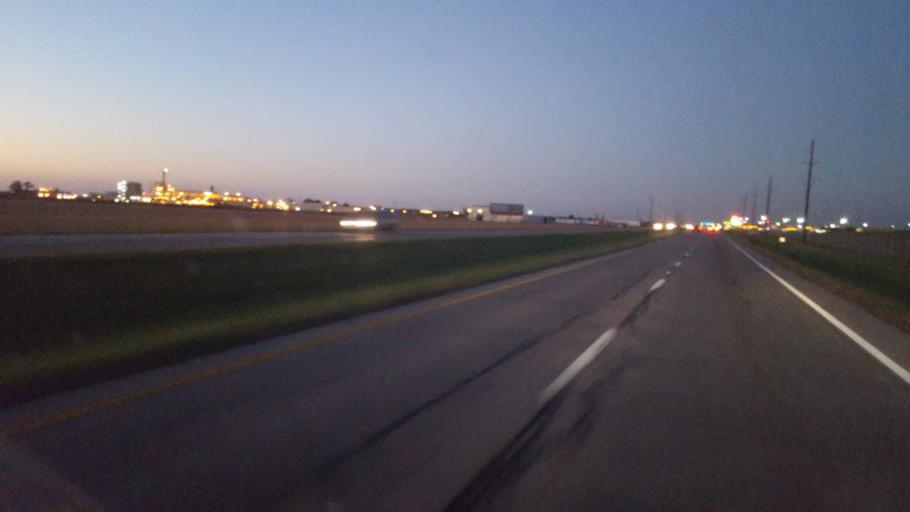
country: US
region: Ohio
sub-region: Pickaway County
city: Logan Elm Village
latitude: 39.5492
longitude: -82.9621
